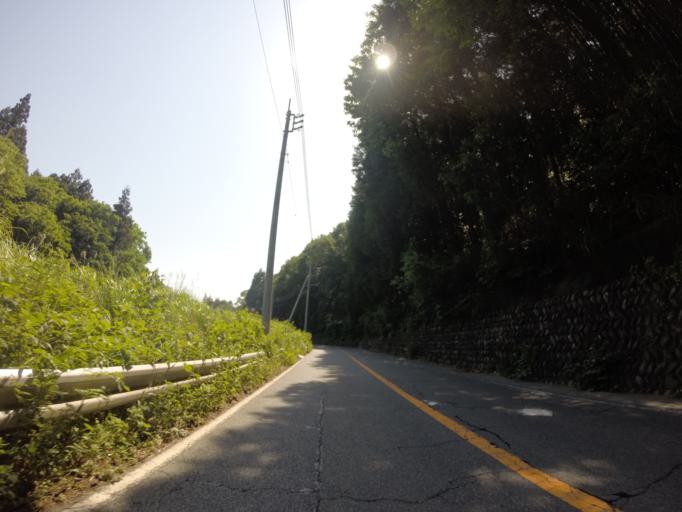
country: JP
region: Shizuoka
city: Fujinomiya
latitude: 35.2028
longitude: 138.6042
